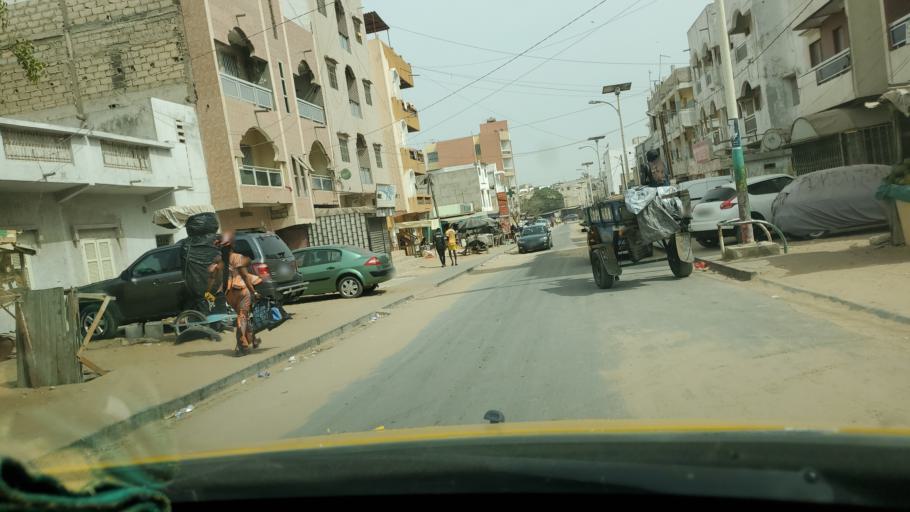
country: SN
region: Dakar
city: Pikine
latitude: 14.7716
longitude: -17.3942
